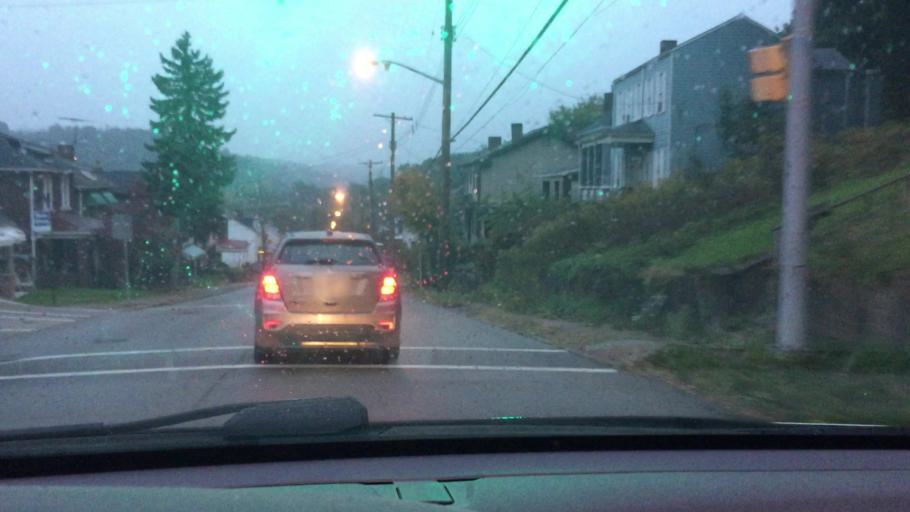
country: US
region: Pennsylvania
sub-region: Allegheny County
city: Crafton
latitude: 40.4428
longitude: -80.0424
